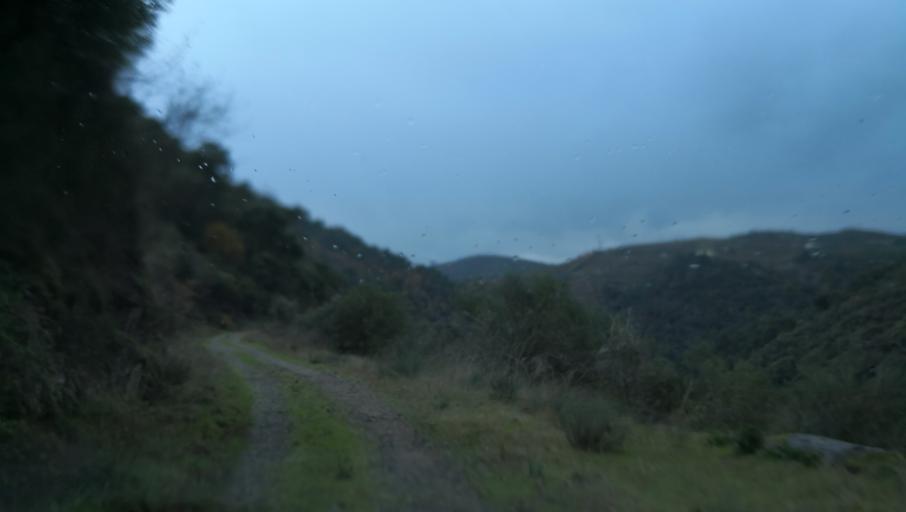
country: PT
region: Vila Real
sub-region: Santa Marta de Penaguiao
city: Santa Marta de Penaguiao
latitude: 41.2166
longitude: -7.7553
